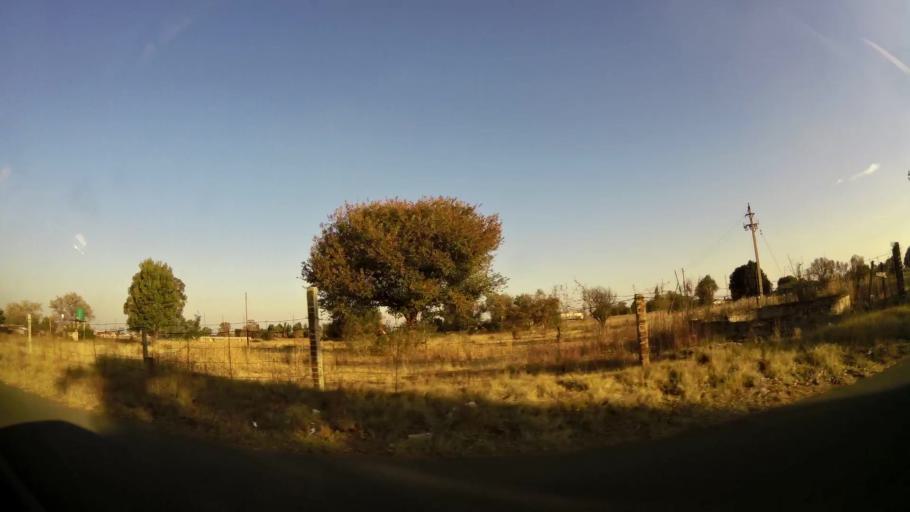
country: ZA
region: Gauteng
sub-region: West Rand District Municipality
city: Randfontein
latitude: -26.2020
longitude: 27.6455
